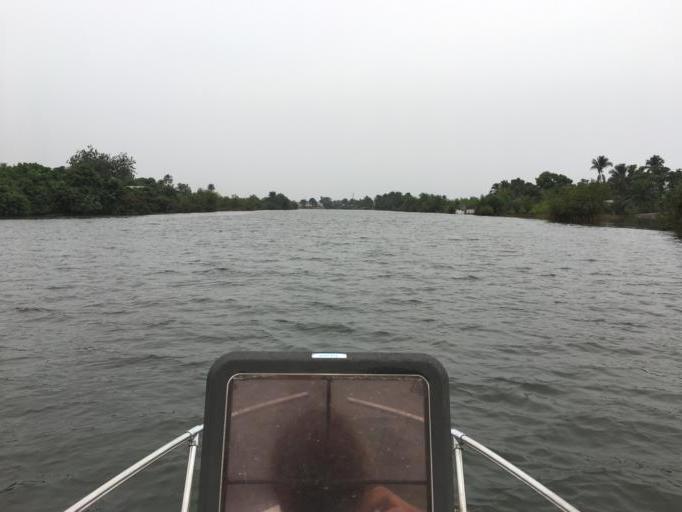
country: LR
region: Montserrado
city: Monrovia
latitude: 6.3894
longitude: -10.7762
